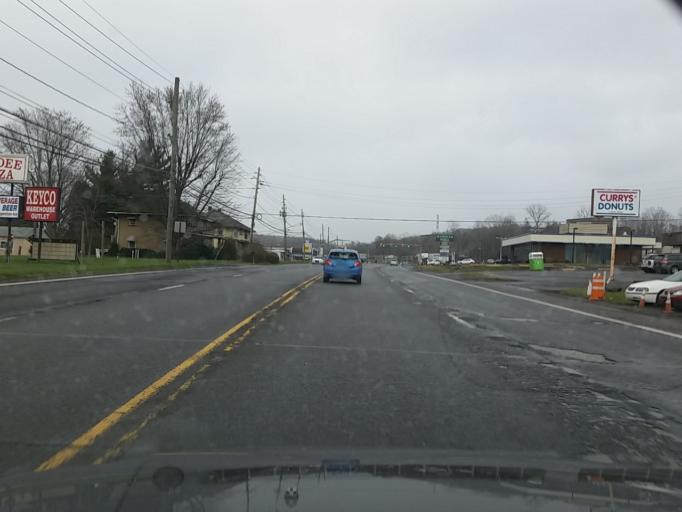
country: US
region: Pennsylvania
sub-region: Luzerne County
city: Nanticoke
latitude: 41.2097
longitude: -75.9740
